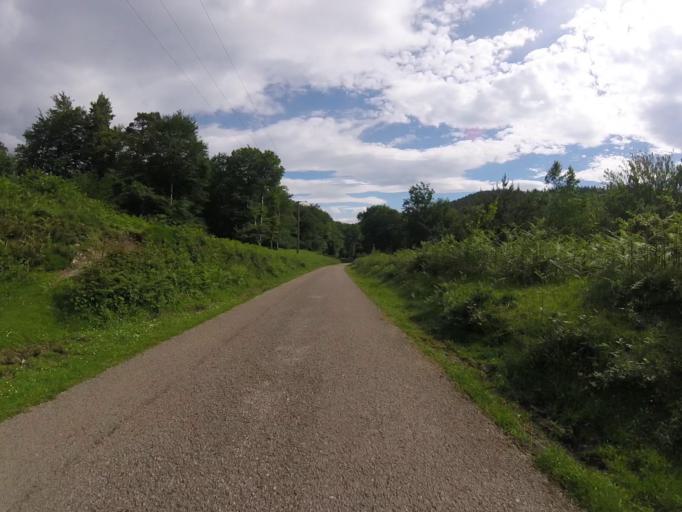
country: ES
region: Navarre
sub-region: Provincia de Navarra
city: Arantza
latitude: 43.2379
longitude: -1.8037
